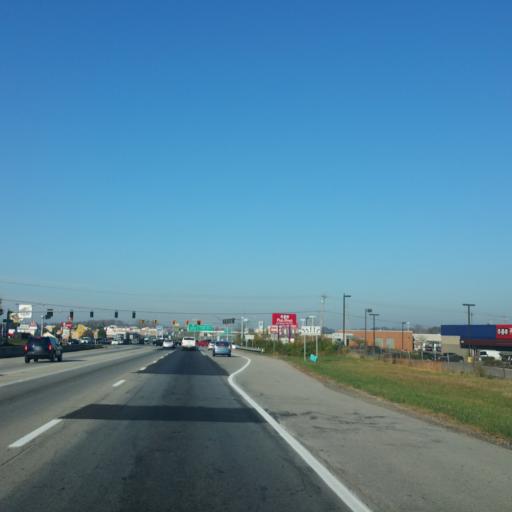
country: US
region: Ohio
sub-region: Clermont County
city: Summerside
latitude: 39.0945
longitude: -84.2613
